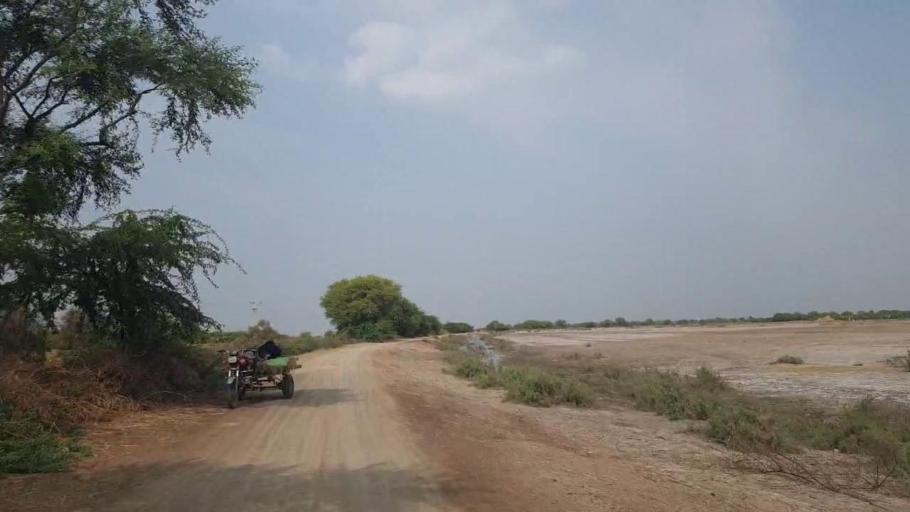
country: PK
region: Sindh
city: Badin
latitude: 24.5528
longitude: 68.7310
